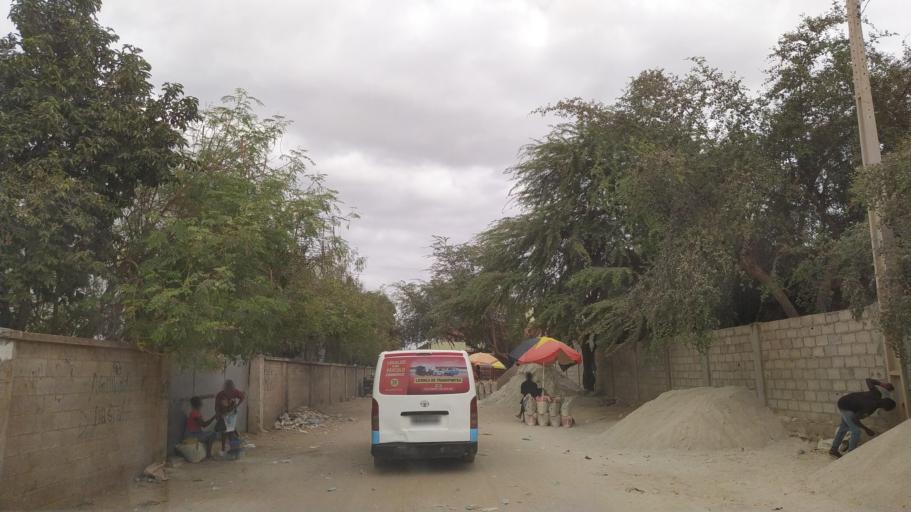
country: AO
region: Luanda
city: Luanda
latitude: -8.9321
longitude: 13.2615
